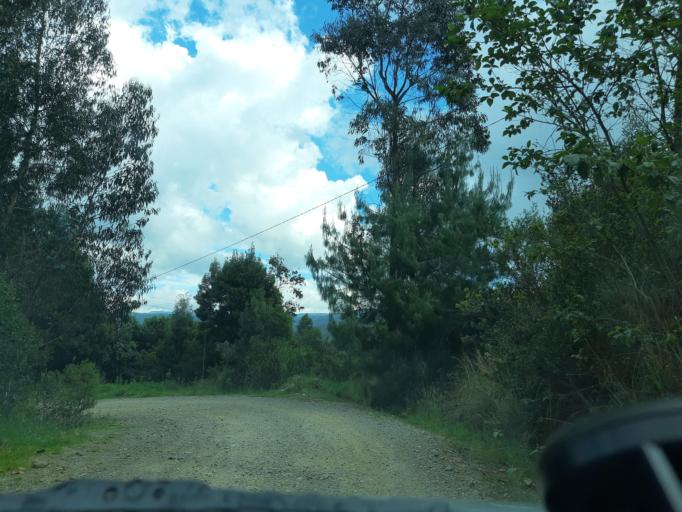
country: CO
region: Boyaca
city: Raquira
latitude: 5.5052
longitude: -73.6718
